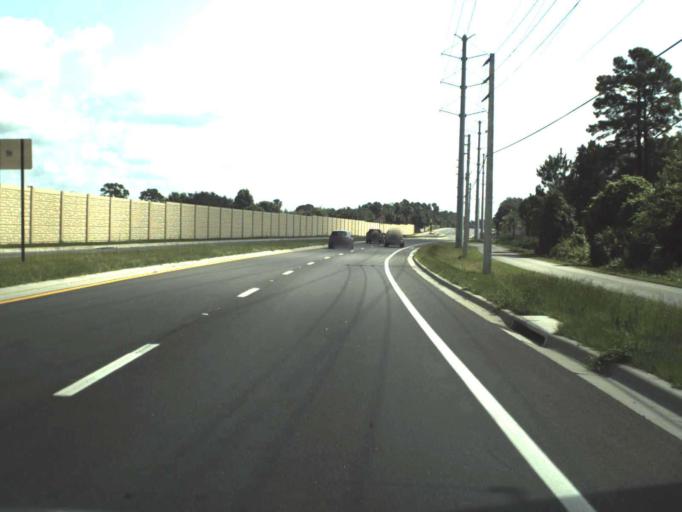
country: US
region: Florida
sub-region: Seminole County
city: Midway
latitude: 28.8348
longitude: -81.1728
